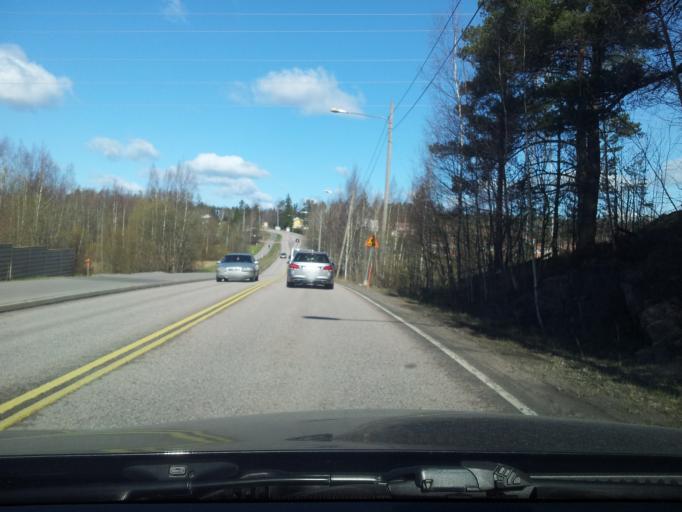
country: FI
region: Uusimaa
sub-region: Helsinki
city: Espoo
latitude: 60.1776
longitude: 24.6850
